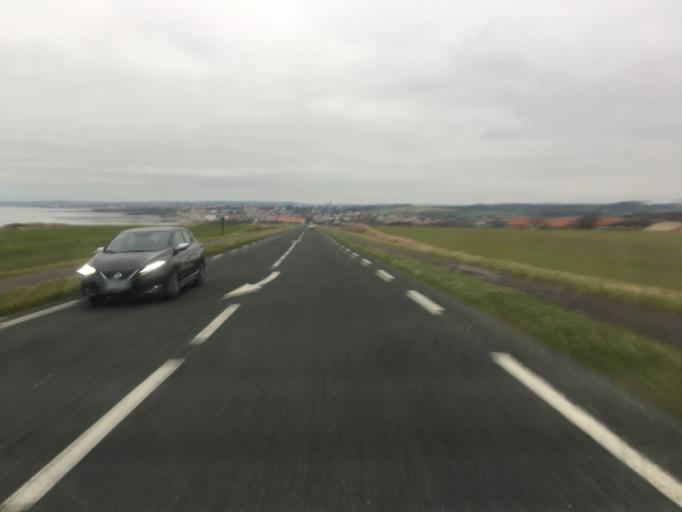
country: FR
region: Nord-Pas-de-Calais
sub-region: Departement du Pas-de-Calais
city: Wimereux
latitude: 50.7507
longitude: 1.6008
